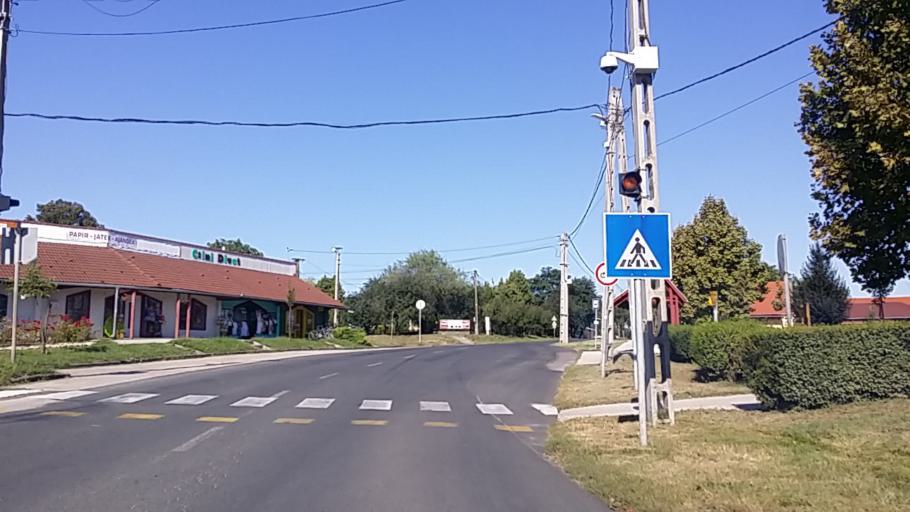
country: HU
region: Fejer
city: Racalmas
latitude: 47.0247
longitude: 18.9335
